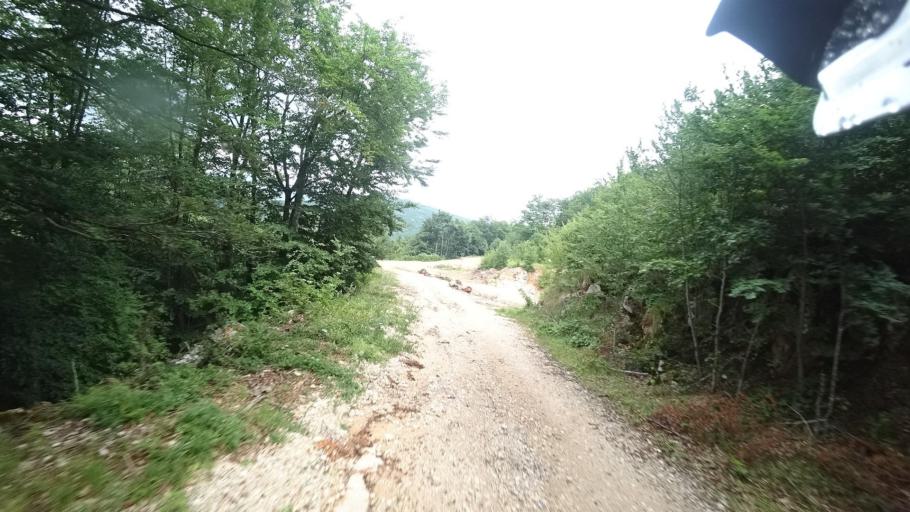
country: BA
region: Federation of Bosnia and Herzegovina
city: Bihac
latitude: 44.6563
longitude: 15.7698
